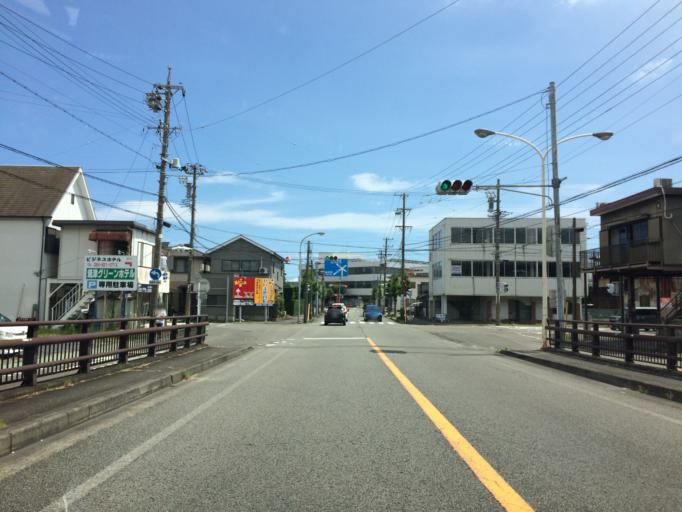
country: JP
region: Shizuoka
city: Yaizu
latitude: 34.8690
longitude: 138.3157
